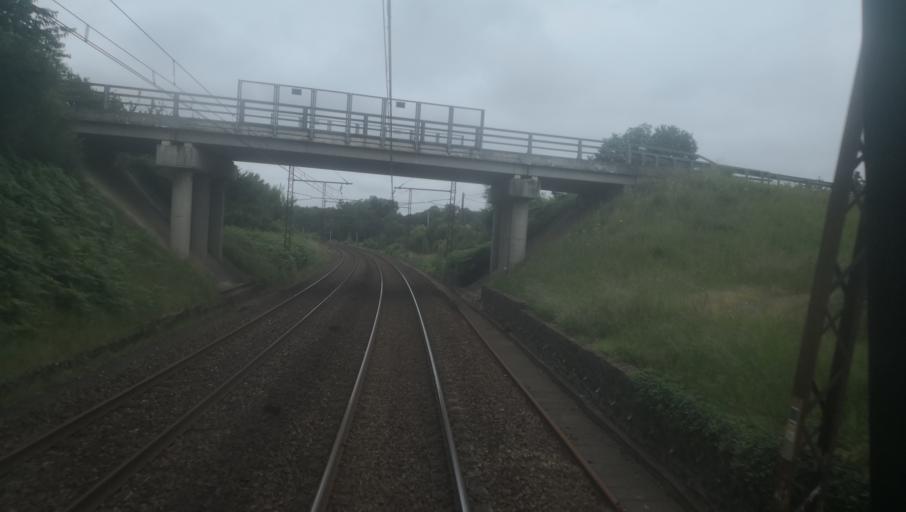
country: FR
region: Centre
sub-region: Departement de l'Indre
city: Chantome
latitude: 46.4925
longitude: 1.5349
